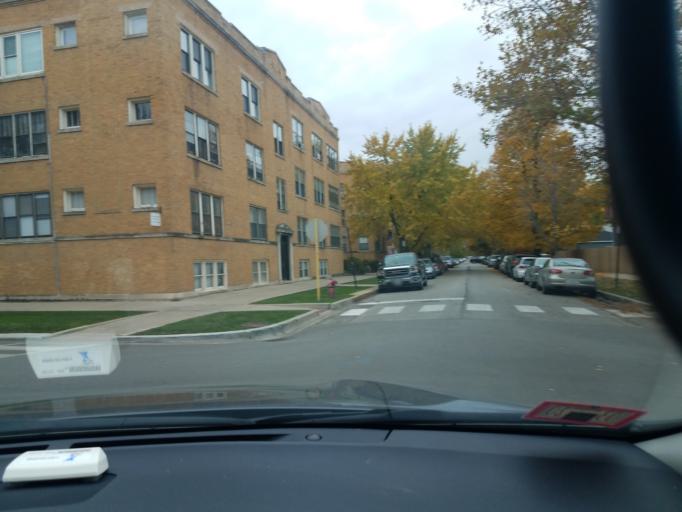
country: US
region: Illinois
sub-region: Cook County
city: Lincolnwood
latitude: 41.9518
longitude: -87.7307
